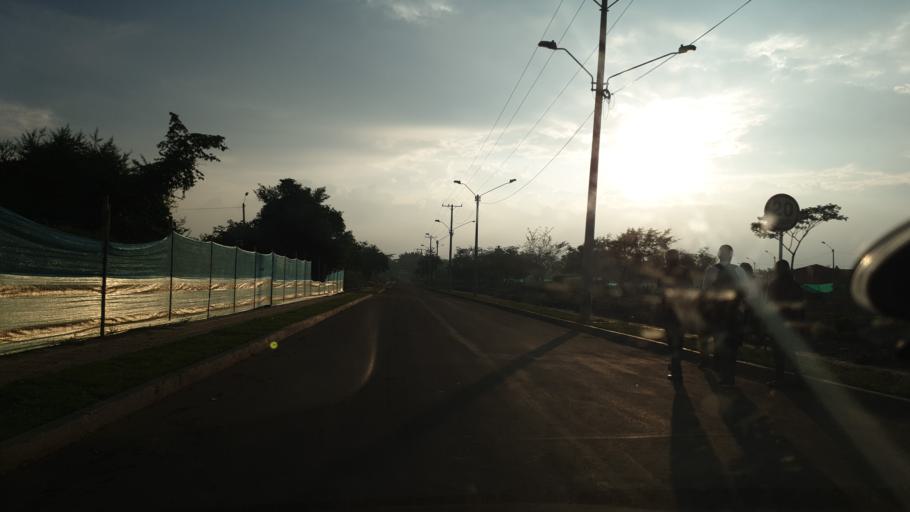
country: CO
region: Valle del Cauca
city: Jamundi
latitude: 3.3452
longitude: -76.5185
